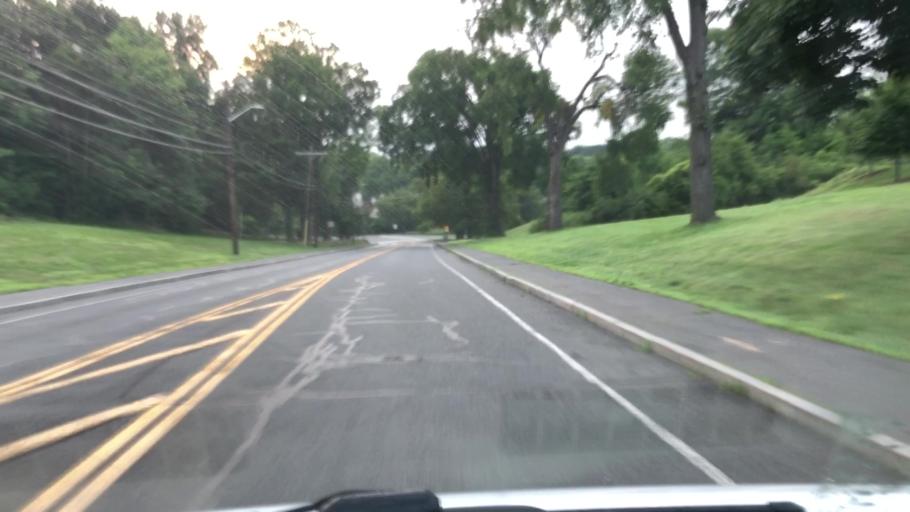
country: US
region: Massachusetts
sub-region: Hampshire County
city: Northampton
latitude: 42.3111
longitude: -72.6459
